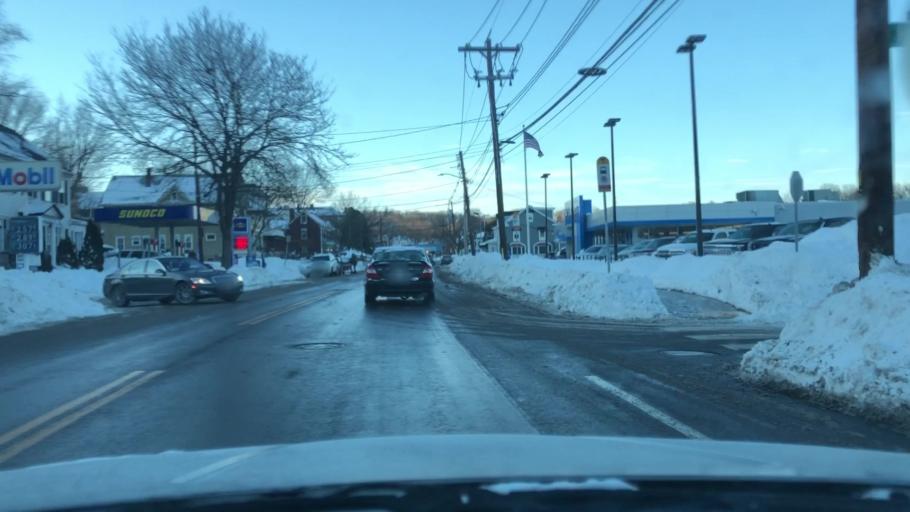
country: US
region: Massachusetts
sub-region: Middlesex County
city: Arlington
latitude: 42.4219
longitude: -71.1726
